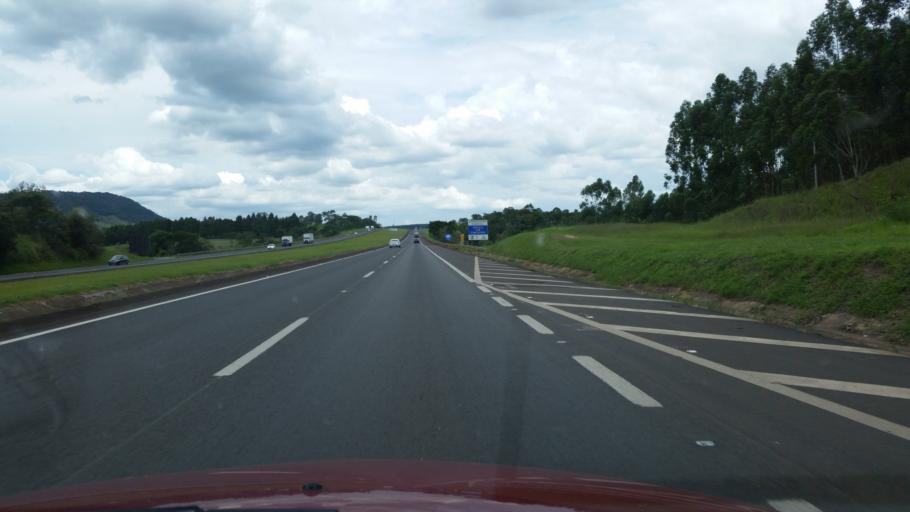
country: BR
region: Sao Paulo
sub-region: Itatinga
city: Itatinga
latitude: -23.1502
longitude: -48.3935
